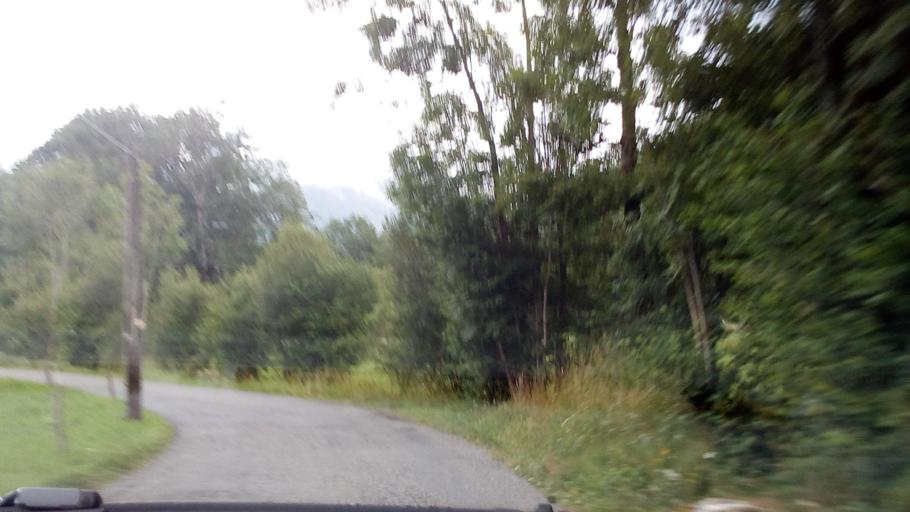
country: FR
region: Midi-Pyrenees
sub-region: Departement des Hautes-Pyrenees
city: Cauterets
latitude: 42.9466
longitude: -0.1892
